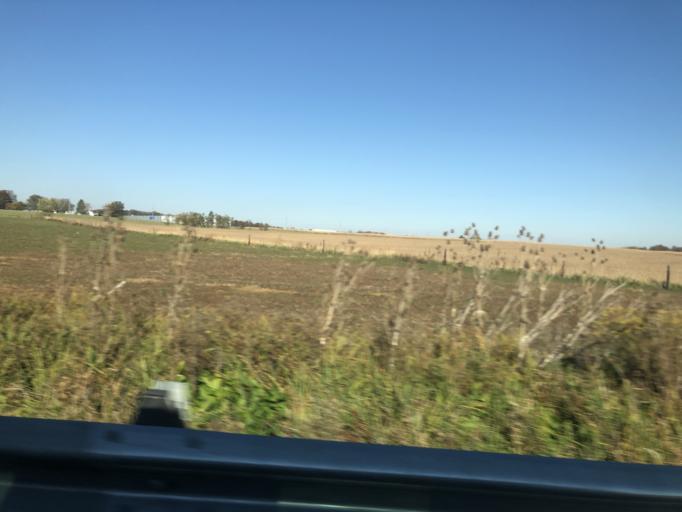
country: US
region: Indiana
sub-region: Allen County
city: Fort Wayne
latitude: 41.1120
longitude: -85.2242
